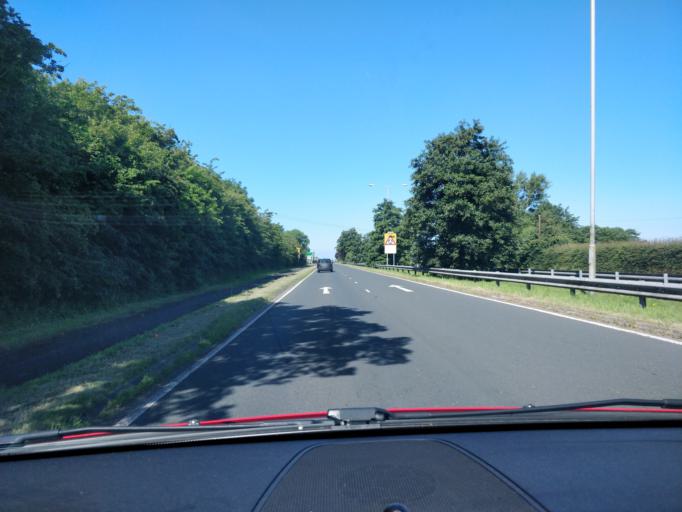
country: GB
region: England
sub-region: Lancashire
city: Banks
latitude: 53.6636
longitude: -2.8791
